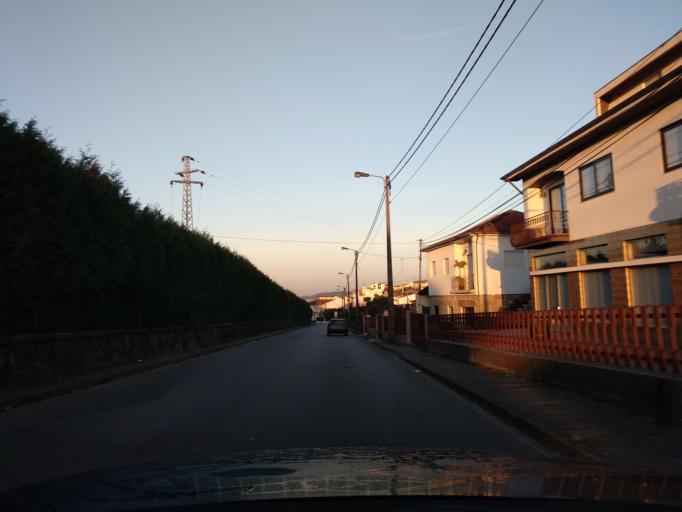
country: PT
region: Porto
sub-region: Paredes
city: Lordelo
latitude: 41.2344
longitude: -8.3783
